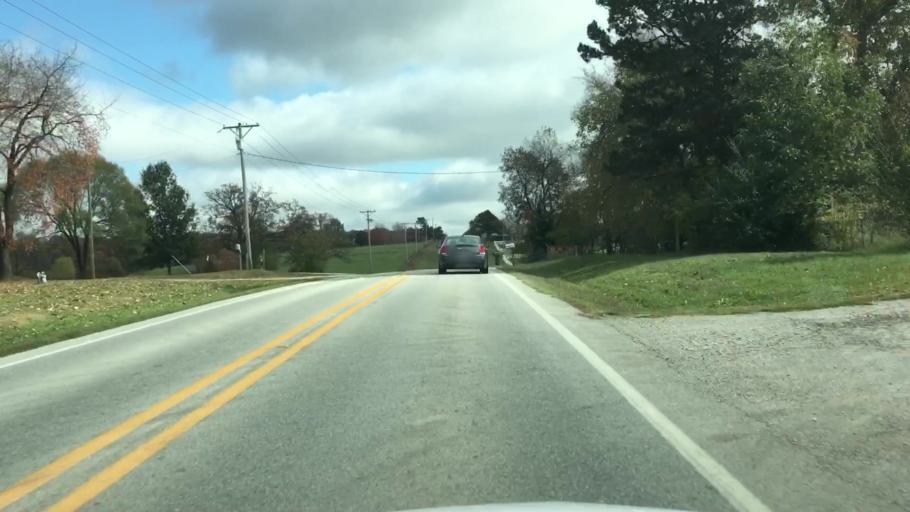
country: US
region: Arkansas
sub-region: Benton County
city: Gentry
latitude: 36.2634
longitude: -94.4597
